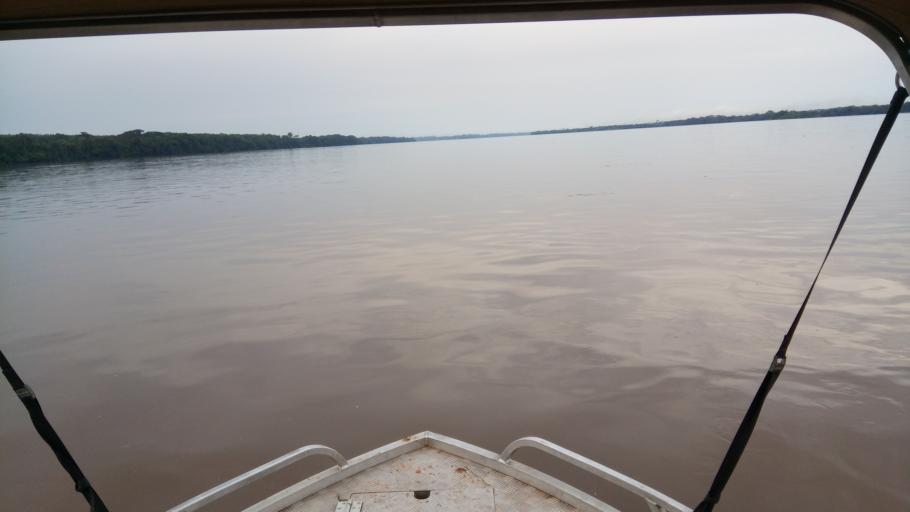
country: CD
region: Eastern Province
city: Kisangani
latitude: 0.5737
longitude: 24.8364
